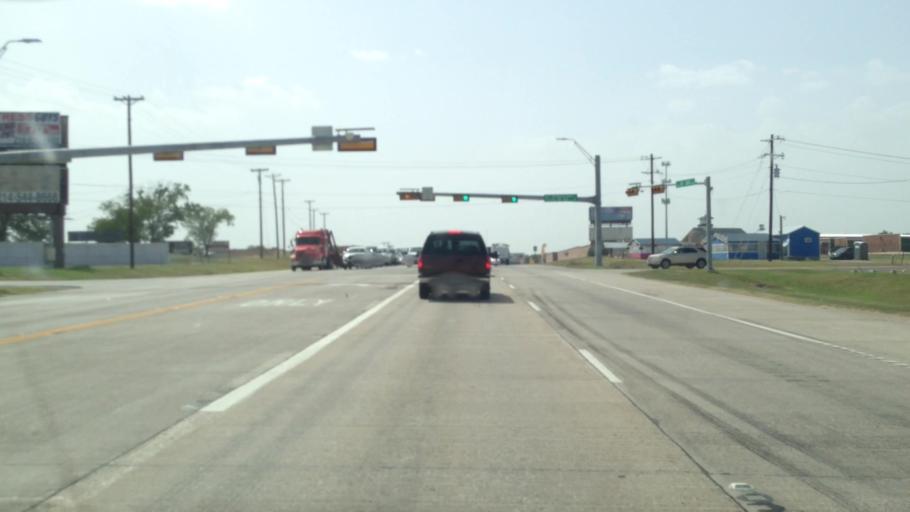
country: US
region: Texas
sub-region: Collin County
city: Lowry Crossing
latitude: 33.1894
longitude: -96.5472
